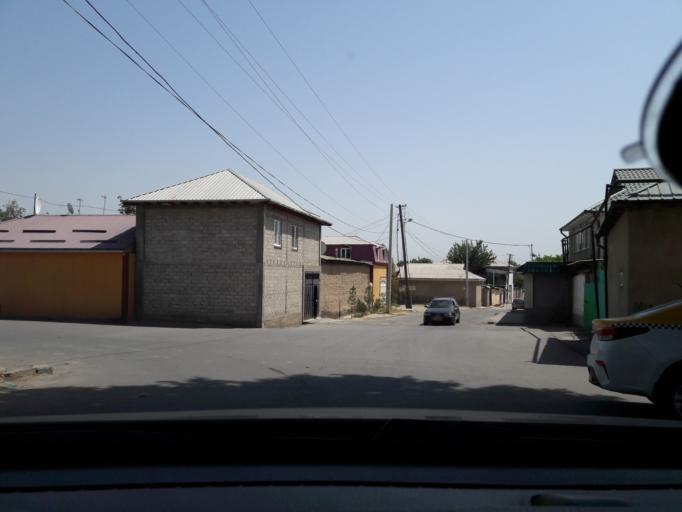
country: TJ
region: Dushanbe
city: Dushanbe
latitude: 38.5860
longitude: 68.7364
